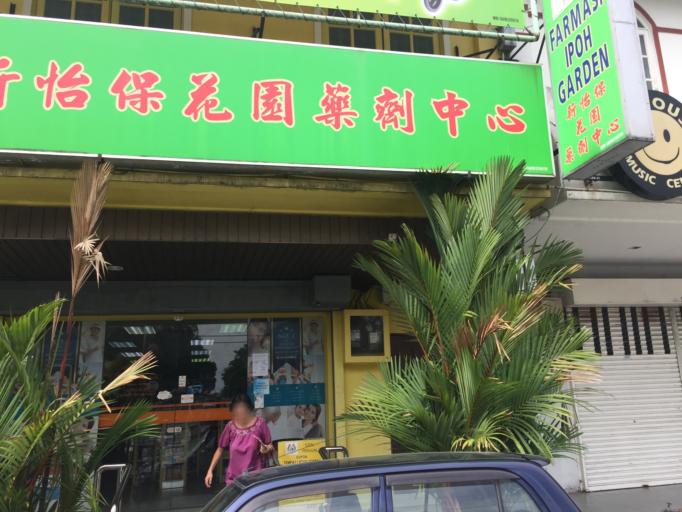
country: MY
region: Perak
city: Ipoh
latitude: 4.6123
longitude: 101.1119
